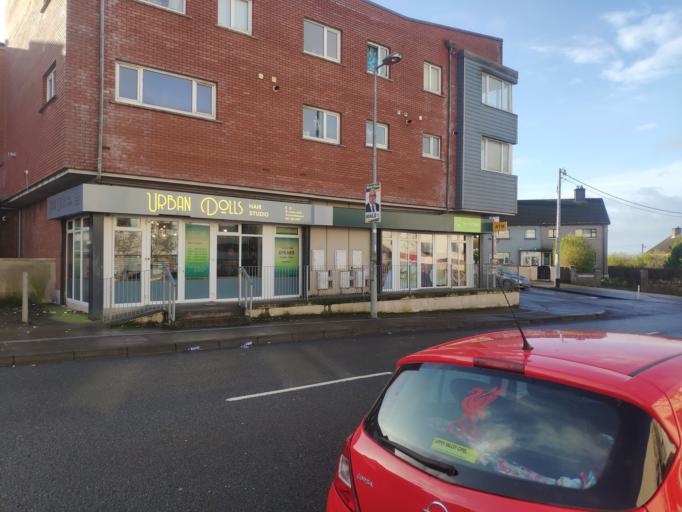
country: IE
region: Munster
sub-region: County Cork
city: Cork
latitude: 51.9112
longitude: -8.4628
